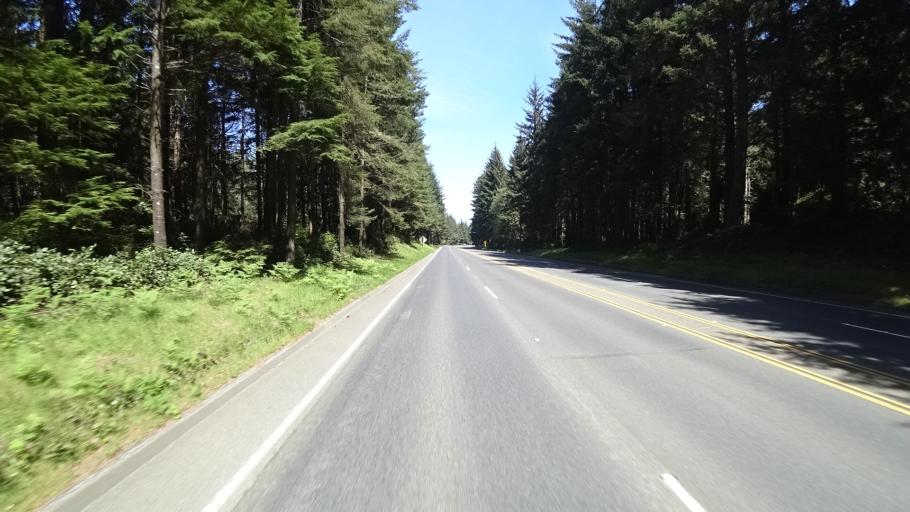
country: US
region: California
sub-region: Humboldt County
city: Westhaven-Moonstone
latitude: 41.1465
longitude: -124.1361
